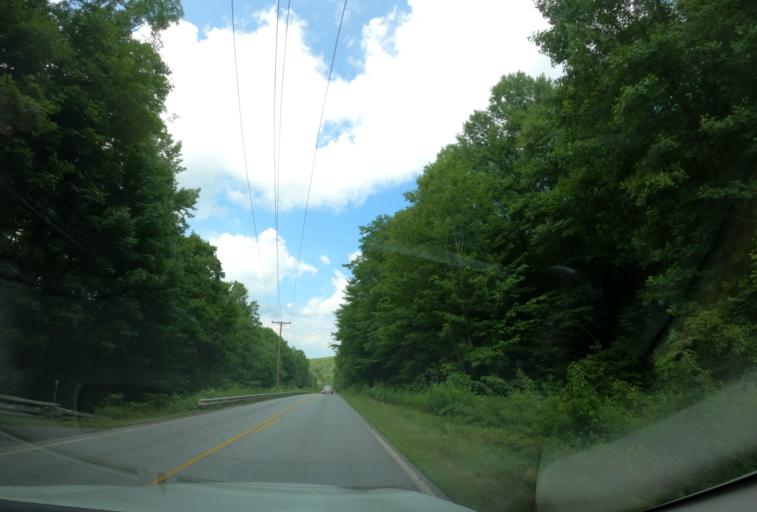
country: US
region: North Carolina
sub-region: Transylvania County
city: Brevard
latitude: 35.0849
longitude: -82.9861
